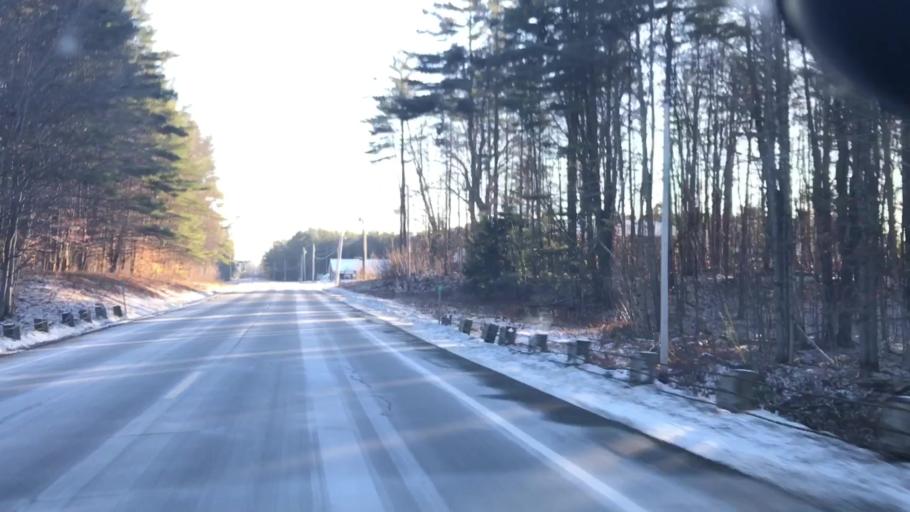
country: US
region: New Hampshire
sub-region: Grafton County
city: Orford
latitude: 43.8747
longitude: -72.1560
